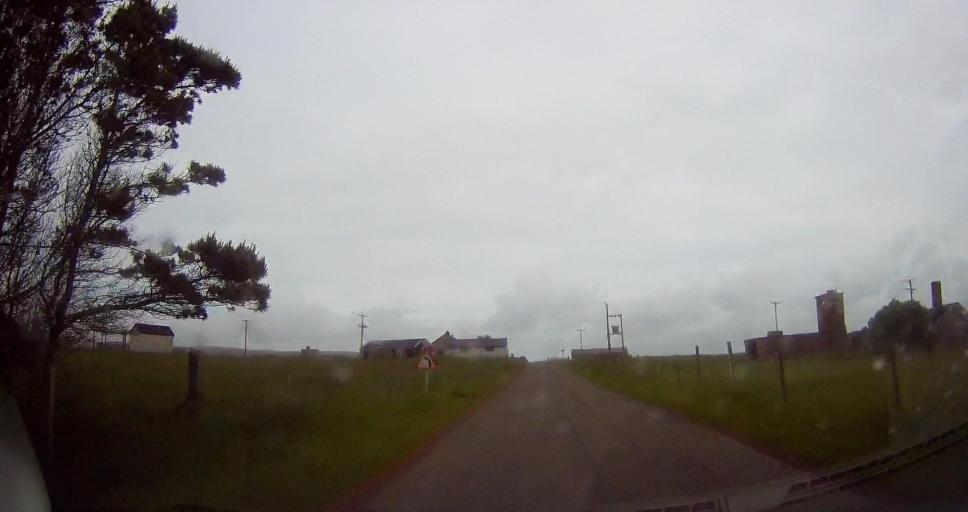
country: GB
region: Scotland
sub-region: Orkney Islands
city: Stromness
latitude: 58.8324
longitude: -3.2066
